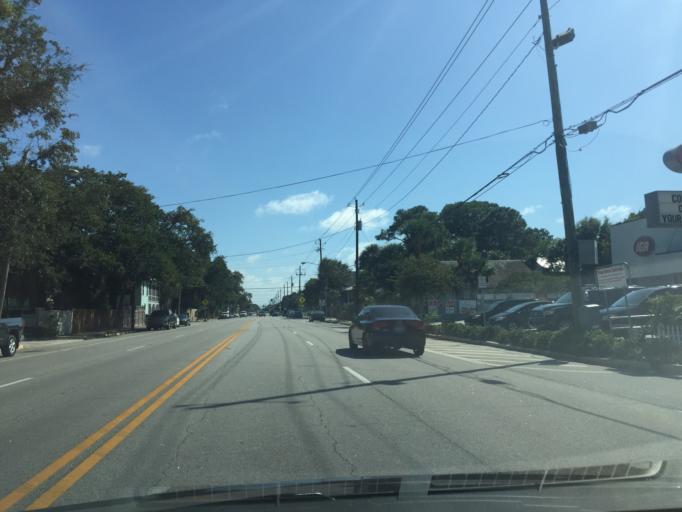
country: US
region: Georgia
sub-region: Chatham County
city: Tybee Island
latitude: 31.9990
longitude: -80.8467
